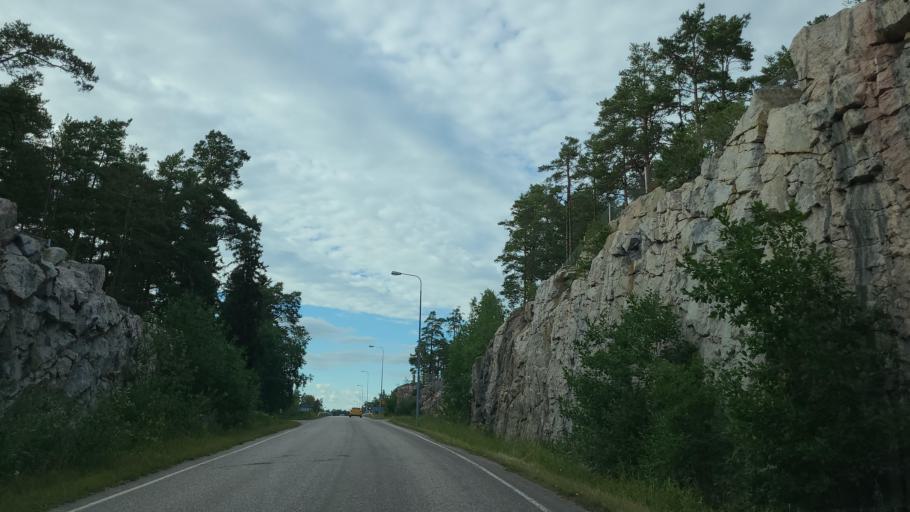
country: FI
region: Varsinais-Suomi
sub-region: Turku
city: Rymaettylae
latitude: 60.3346
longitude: 21.9802
